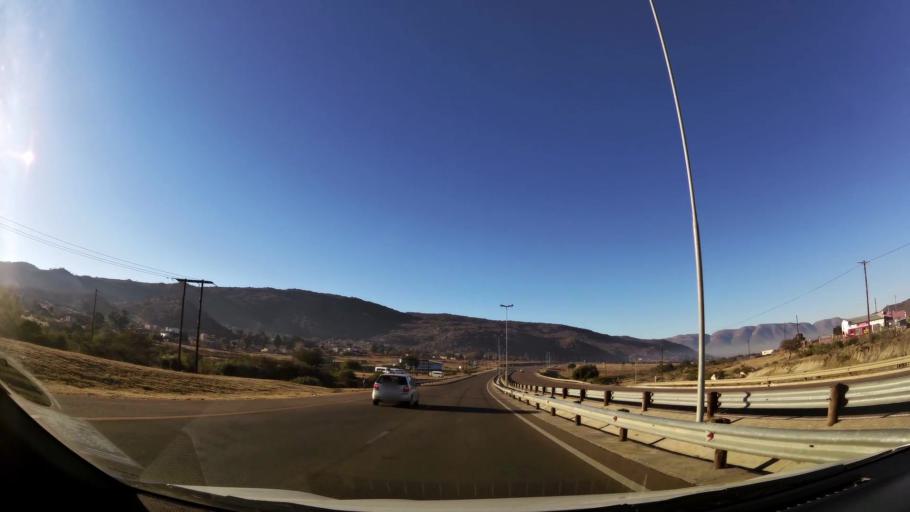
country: ZA
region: Limpopo
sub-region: Capricorn District Municipality
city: Mankoeng
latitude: -23.9174
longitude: 29.7917
